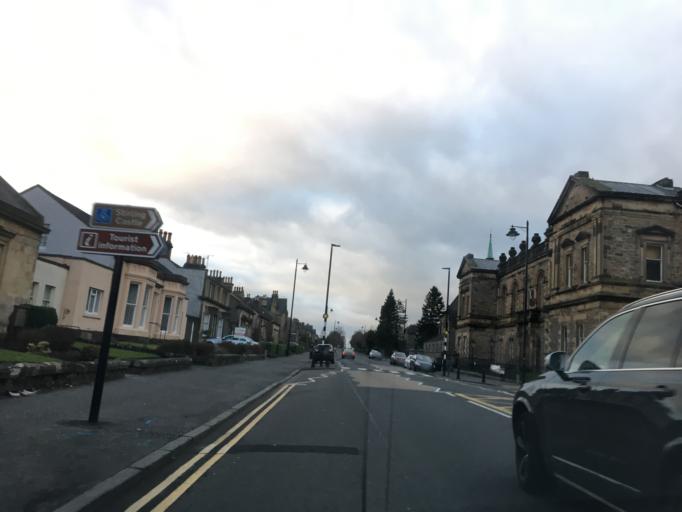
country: GB
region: Scotland
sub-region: Stirling
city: Stirling
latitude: 56.1177
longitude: -3.9410
